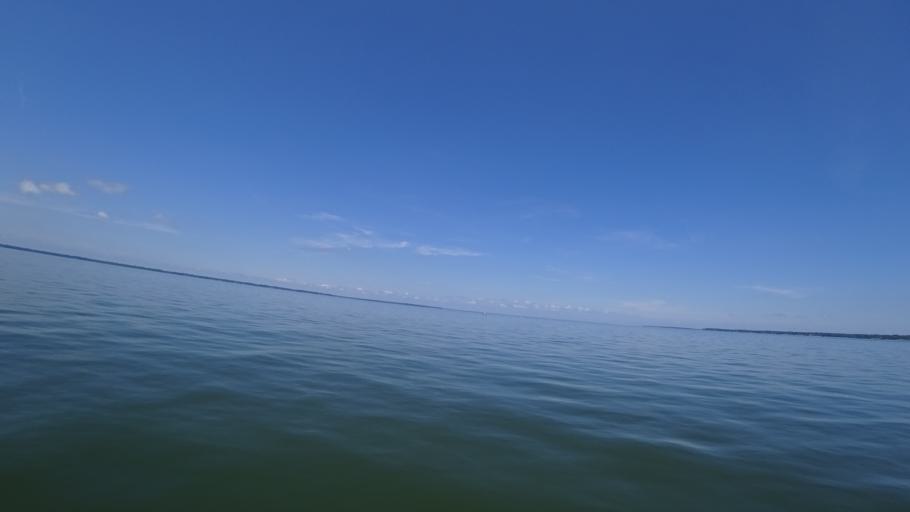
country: US
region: Virginia
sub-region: City of Newport News
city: Newport News
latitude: 37.0053
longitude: -76.4731
